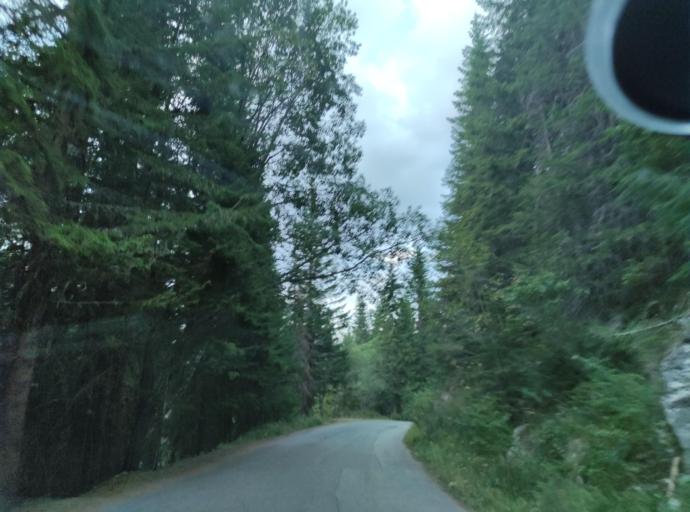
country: BG
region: Blagoevgrad
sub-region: Obshtina Bansko
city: Bansko
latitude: 41.7706
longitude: 23.4293
